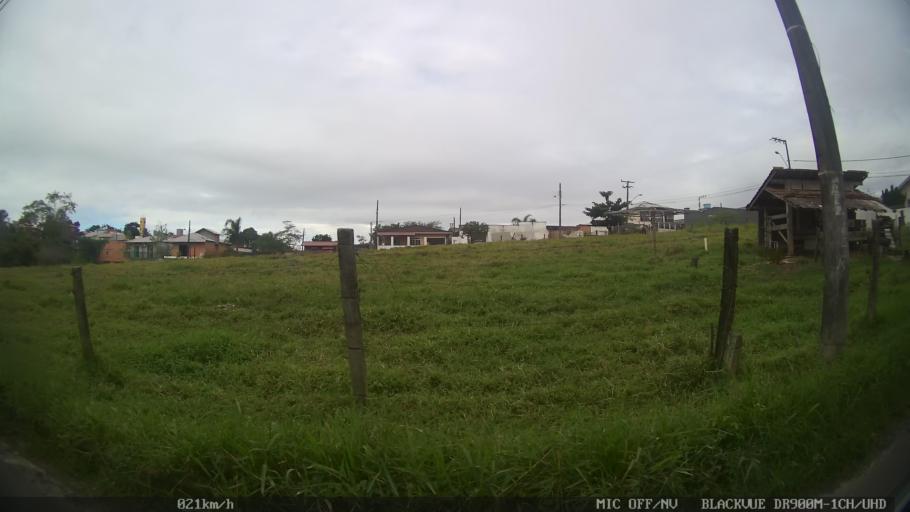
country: BR
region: Santa Catarina
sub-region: Biguacu
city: Biguacu
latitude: -27.5382
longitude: -48.6380
